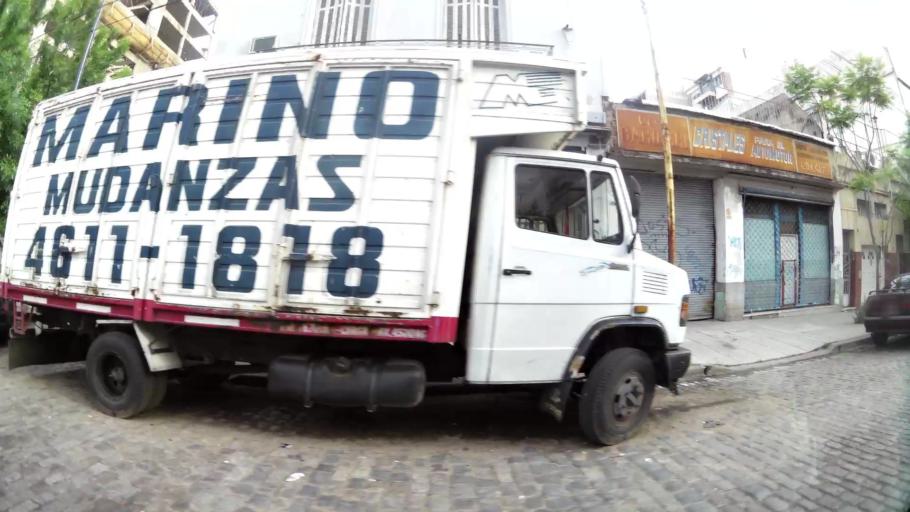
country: AR
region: Buenos Aires F.D.
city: Villa Santa Rita
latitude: -34.6337
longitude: -58.4695
